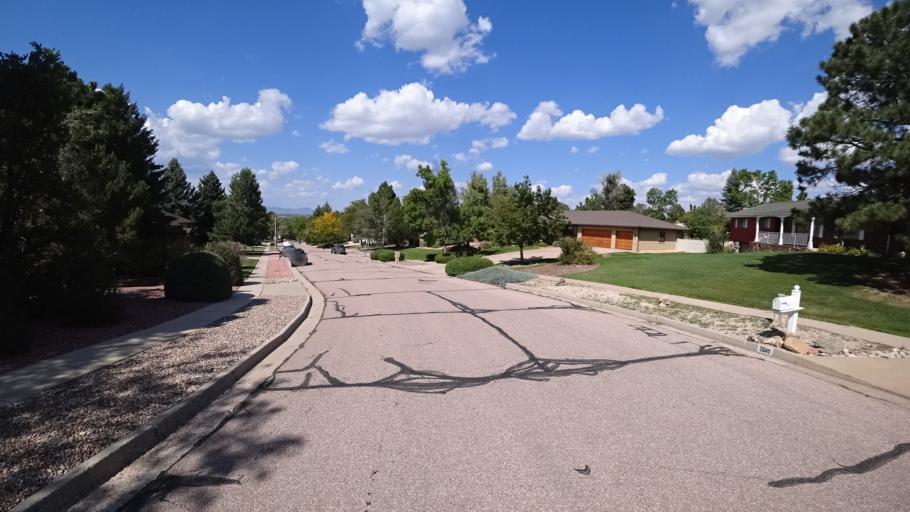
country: US
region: Colorado
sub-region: El Paso County
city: Cimarron Hills
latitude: 38.8725
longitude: -104.7412
